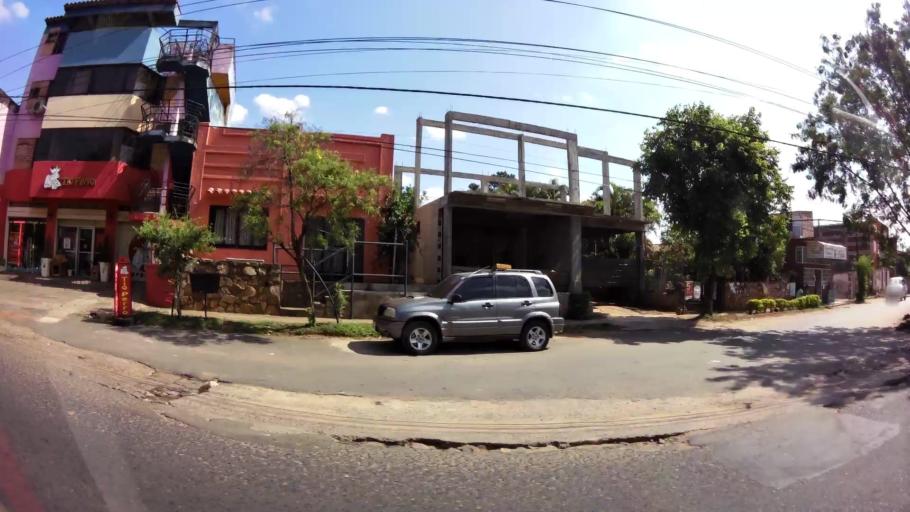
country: PY
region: Central
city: Fernando de la Mora
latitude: -25.3452
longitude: -57.5159
